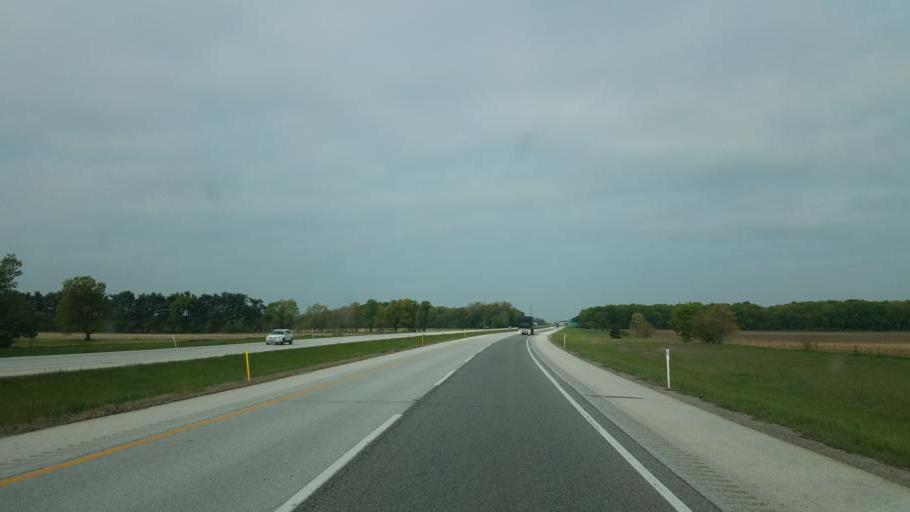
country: US
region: Indiana
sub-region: Elkhart County
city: Bristol
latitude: 41.7317
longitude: -85.8468
